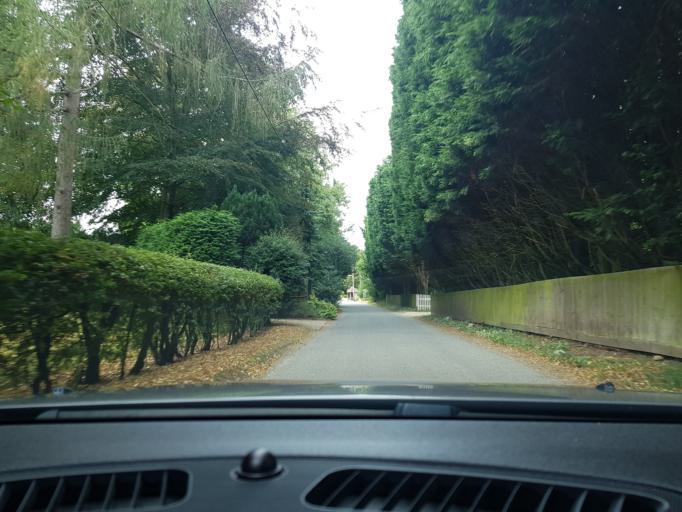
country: GB
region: England
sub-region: West Berkshire
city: Hungerford
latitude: 51.4405
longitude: -1.4872
